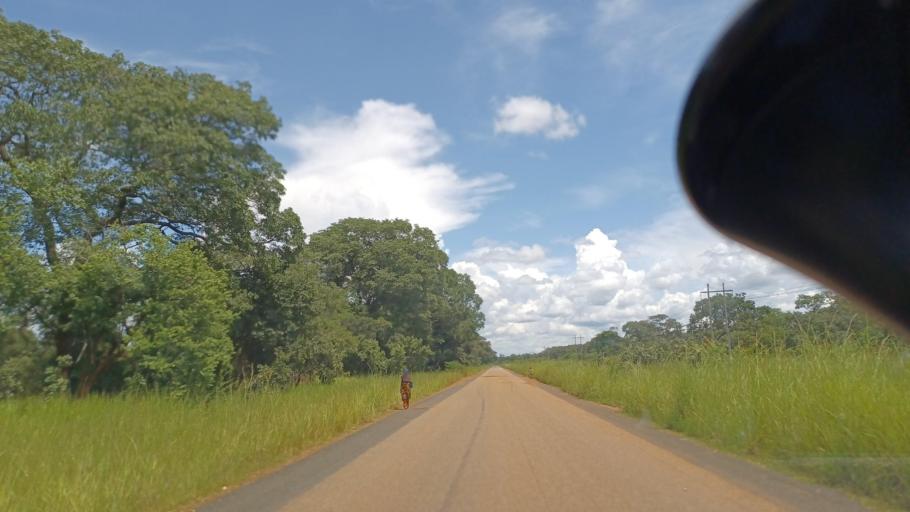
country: ZM
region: North-Western
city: Solwezi
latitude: -12.5733
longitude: 26.1344
